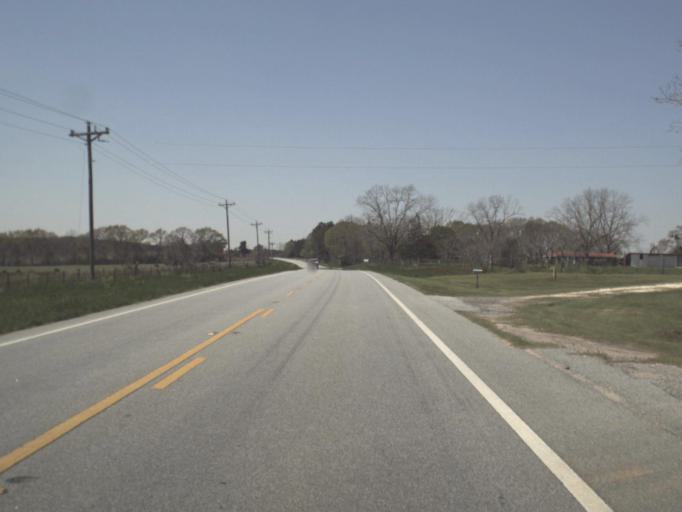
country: US
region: Alabama
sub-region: Geneva County
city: Geneva
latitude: 30.9451
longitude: -85.7700
